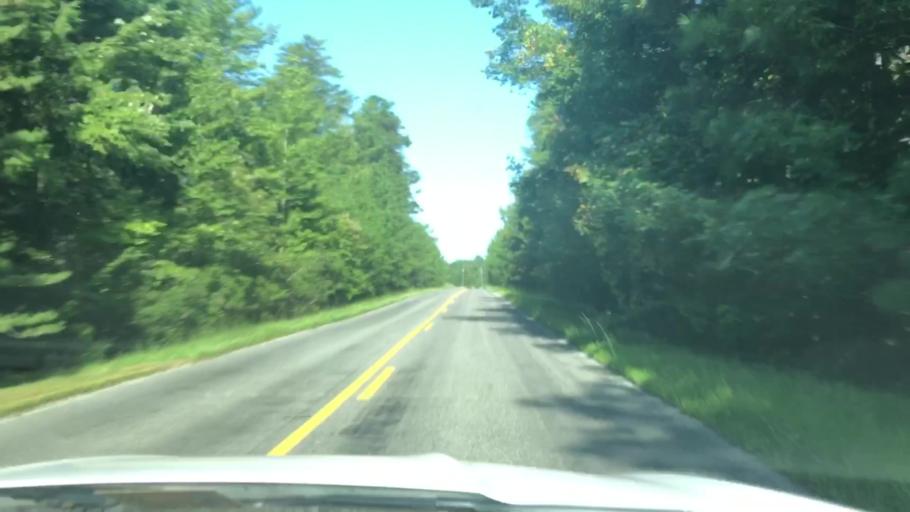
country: US
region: Virginia
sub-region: New Kent County
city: New Kent
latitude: 37.4846
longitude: -76.9293
